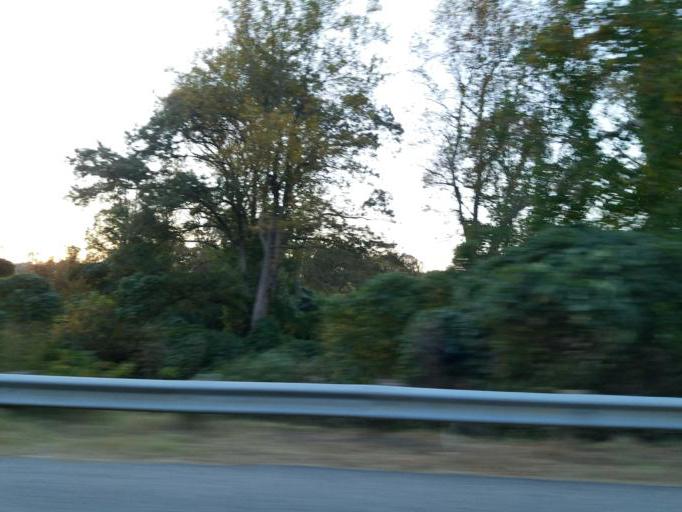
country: US
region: Georgia
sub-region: Dawson County
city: Dawsonville
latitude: 34.3201
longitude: -84.0618
